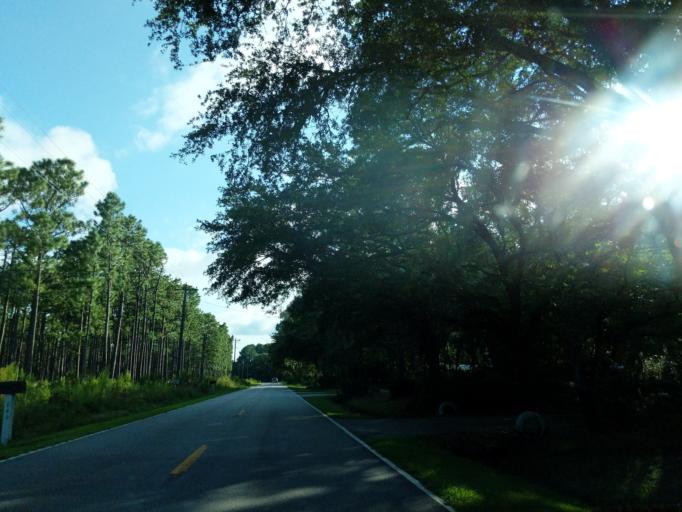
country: US
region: South Carolina
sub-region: Charleston County
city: Awendaw
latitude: 33.1486
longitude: -79.4136
